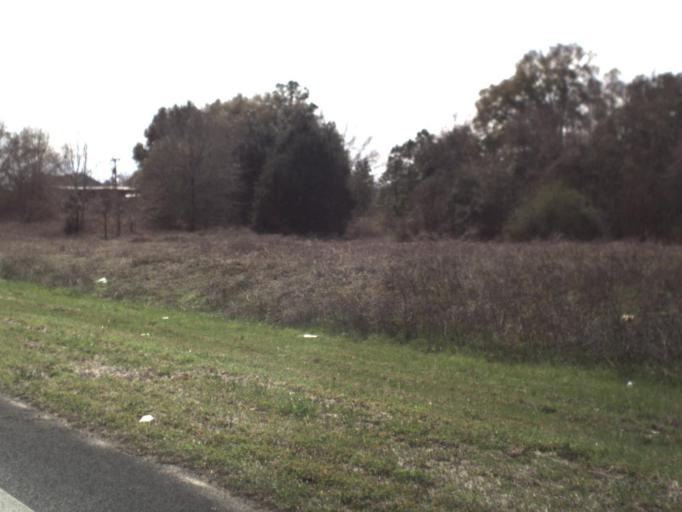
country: US
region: Florida
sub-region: Jackson County
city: Marianna
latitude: 30.7834
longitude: -85.3755
